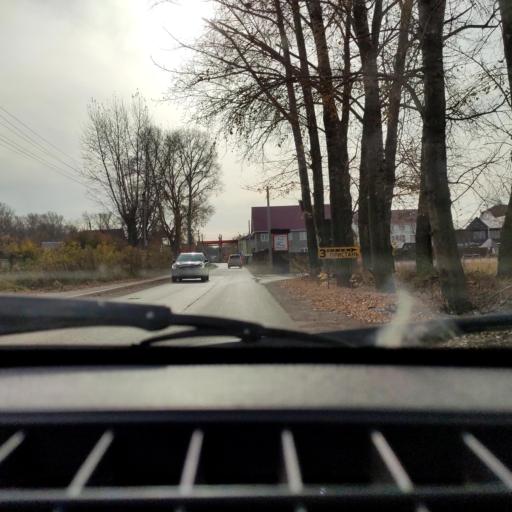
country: RU
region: Bashkortostan
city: Ufa
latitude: 54.6893
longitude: 55.9608
